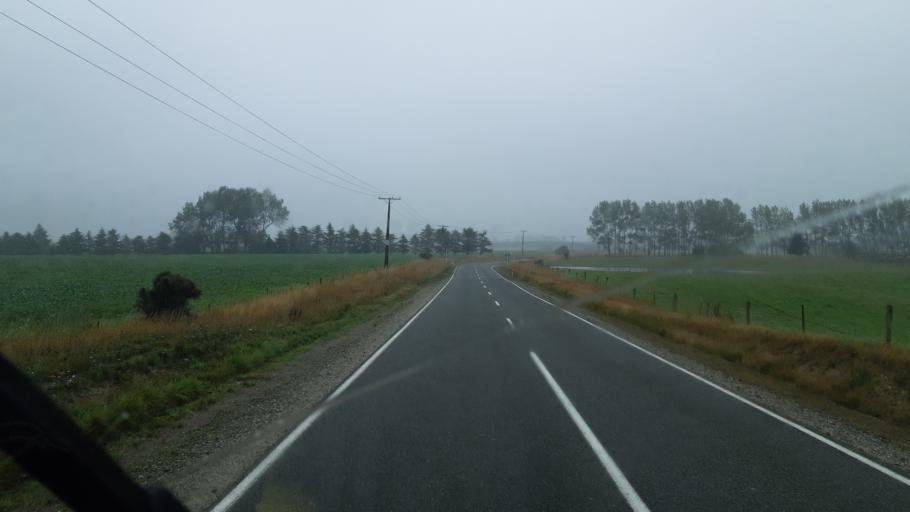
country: NZ
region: Otago
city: Oamaru
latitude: -44.9270
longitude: 170.8124
